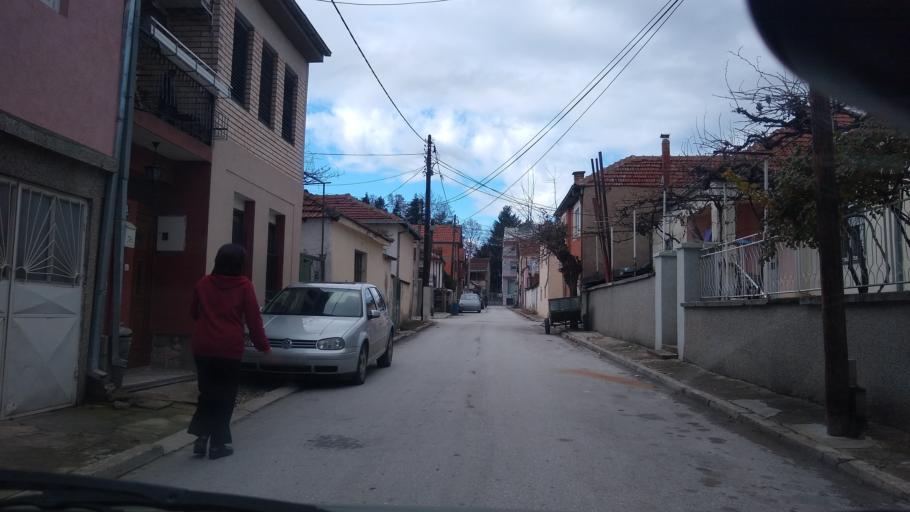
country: MK
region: Bitola
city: Bitola
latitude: 41.0316
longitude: 21.3173
